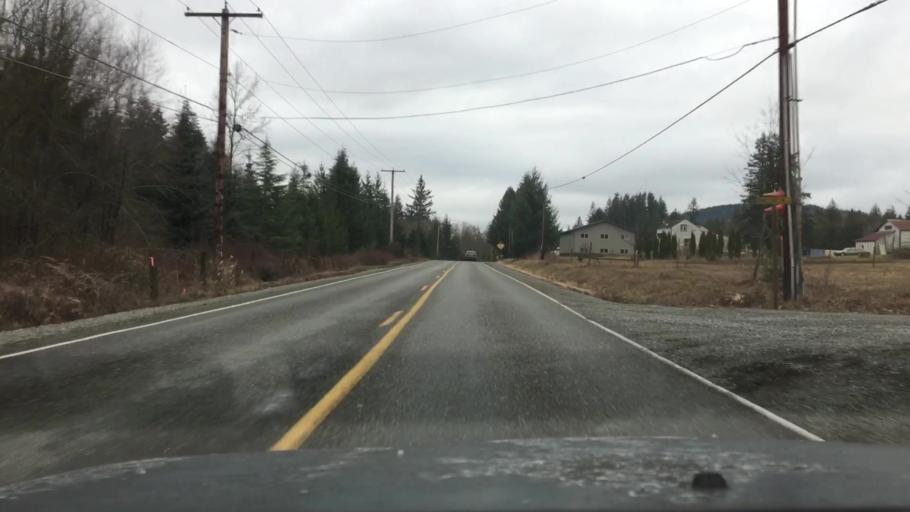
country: US
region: Washington
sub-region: Whatcom County
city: Sudden Valley
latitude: 48.6241
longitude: -122.3243
